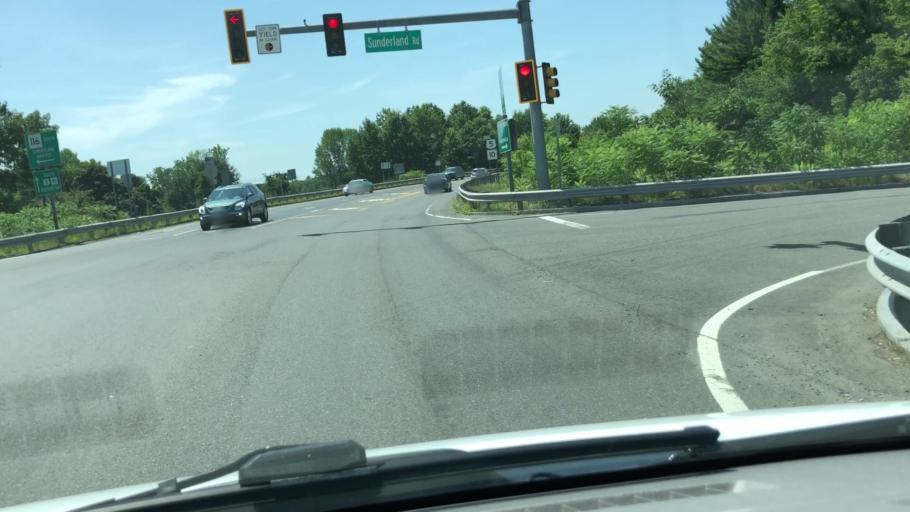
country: US
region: Massachusetts
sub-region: Franklin County
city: South Deerfield
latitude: 42.4692
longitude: -72.6147
